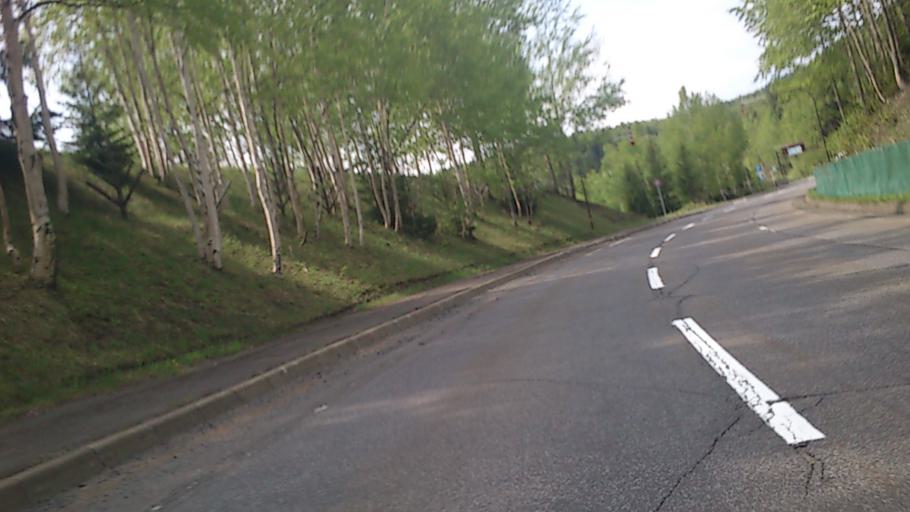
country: JP
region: Hokkaido
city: Kamikawa
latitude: 43.6671
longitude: 143.0373
